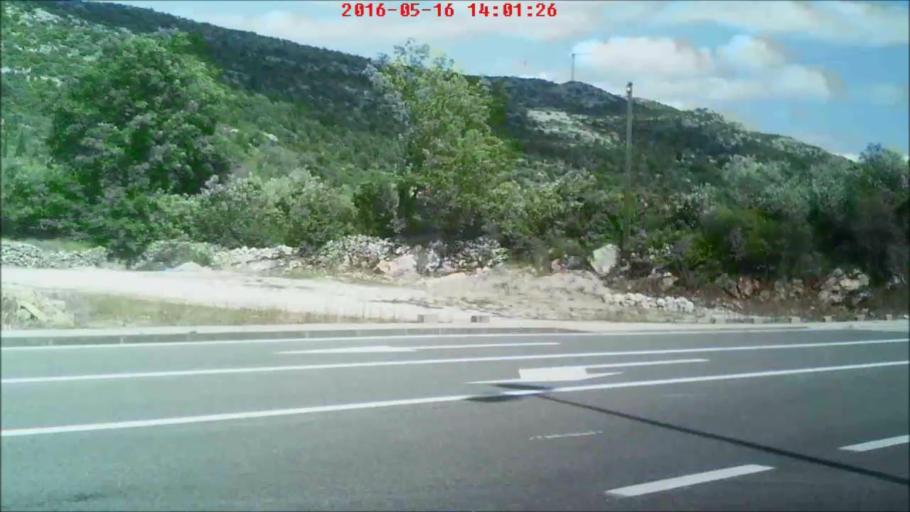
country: HR
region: Dubrovacko-Neretvanska
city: Ston
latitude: 42.8320
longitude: 17.7500
